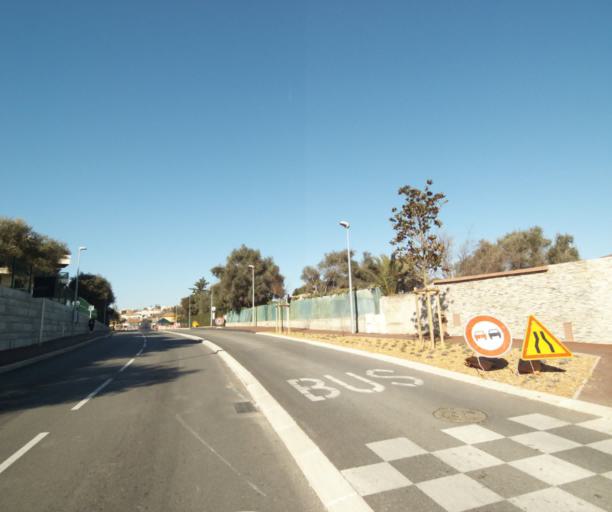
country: FR
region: Provence-Alpes-Cote d'Azur
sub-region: Departement des Alpes-Maritimes
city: Biot
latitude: 43.5945
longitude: 7.1081
